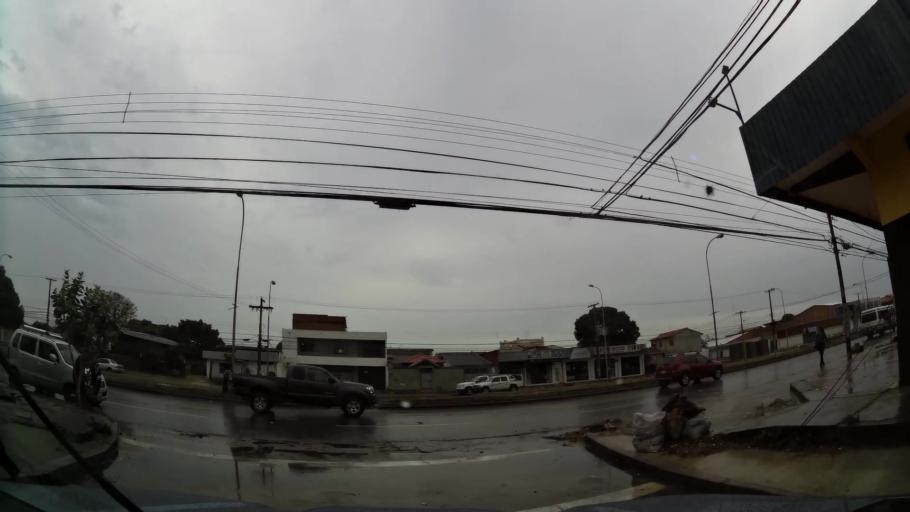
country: BO
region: Santa Cruz
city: Santa Cruz de la Sierra
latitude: -17.7802
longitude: -63.1509
